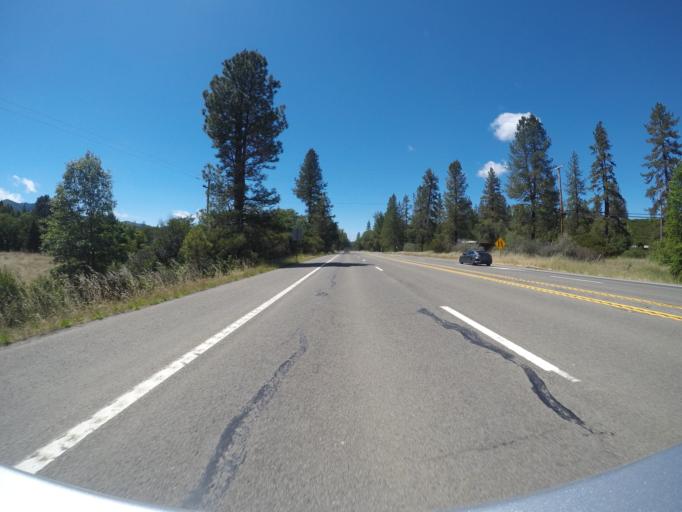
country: US
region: California
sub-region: Mendocino County
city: Laytonville
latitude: 39.7297
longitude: -123.5075
